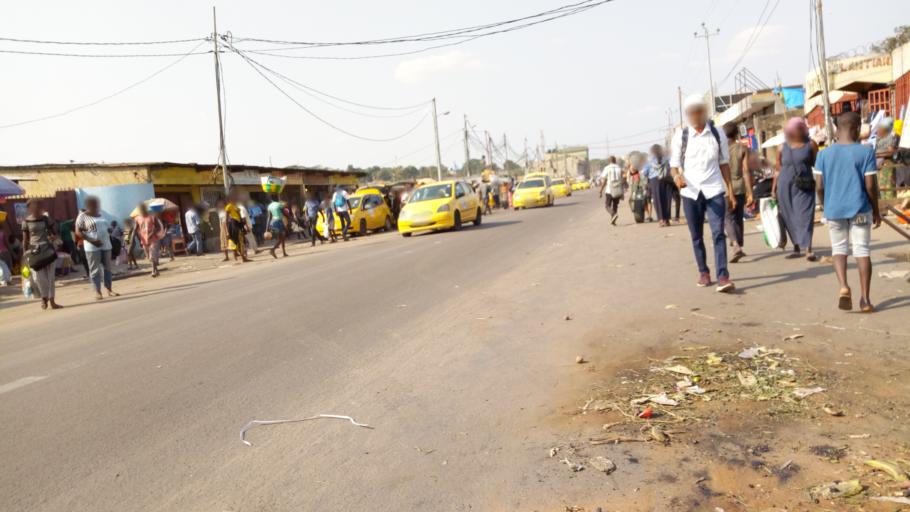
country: CD
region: Kinshasa
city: Kinshasa
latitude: -4.4496
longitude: 15.2478
